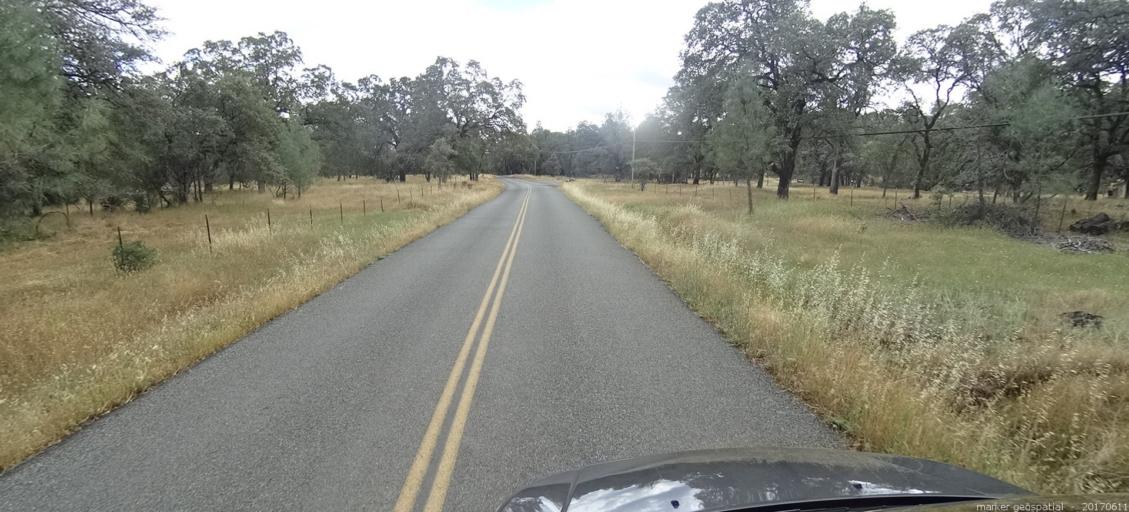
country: US
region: California
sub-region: Butte County
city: Oroville
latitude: 39.6231
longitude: -121.5283
